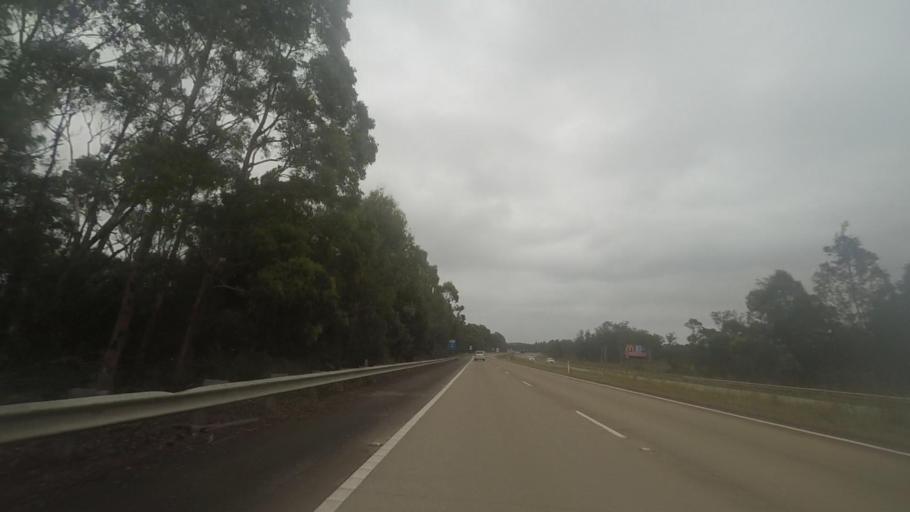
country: AU
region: New South Wales
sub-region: Port Stephens Shire
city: Medowie
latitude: -32.6519
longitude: 151.8815
